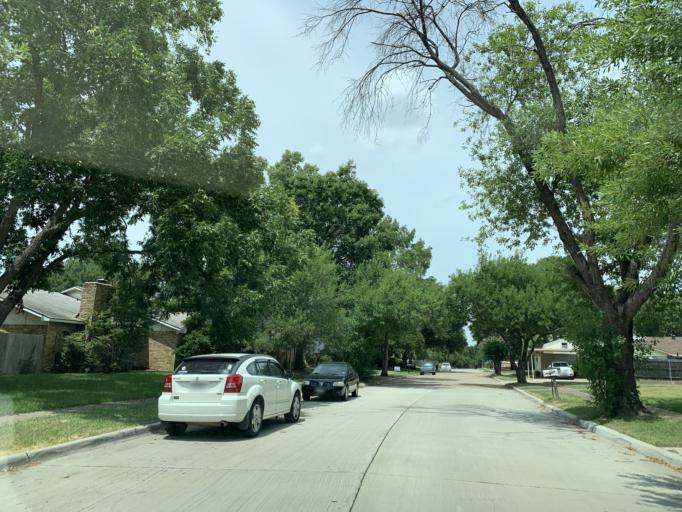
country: US
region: Texas
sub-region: Dallas County
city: Grand Prairie
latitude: 32.6588
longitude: -97.0318
